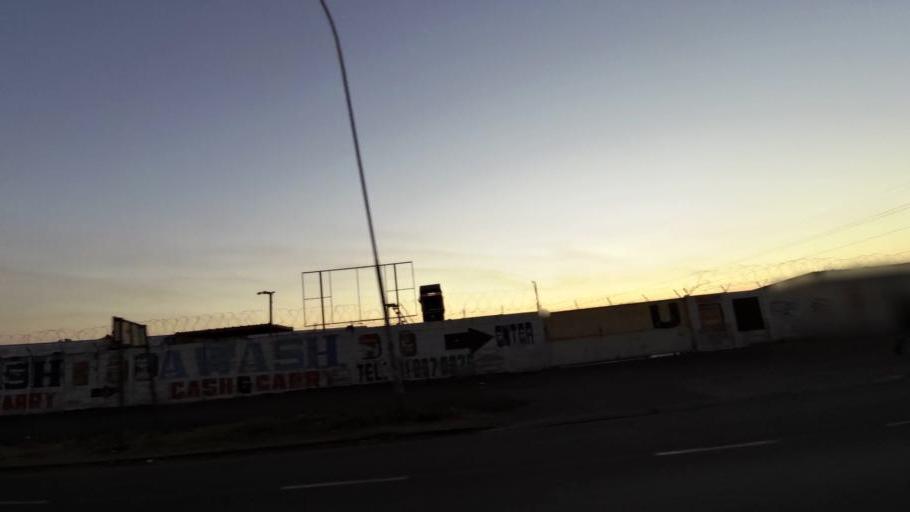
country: ZA
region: Gauteng
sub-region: City of Johannesburg Metropolitan Municipality
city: Johannesburg
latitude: -26.2128
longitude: 28.0101
